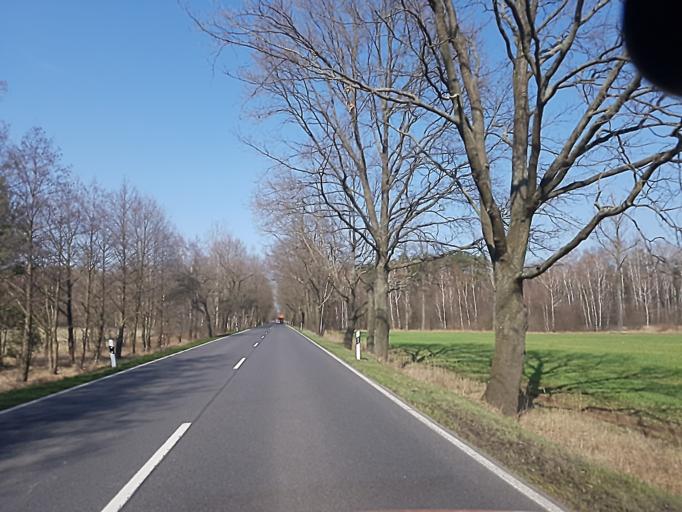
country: DE
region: Brandenburg
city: Tschernitz
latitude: 51.6577
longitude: 14.5898
